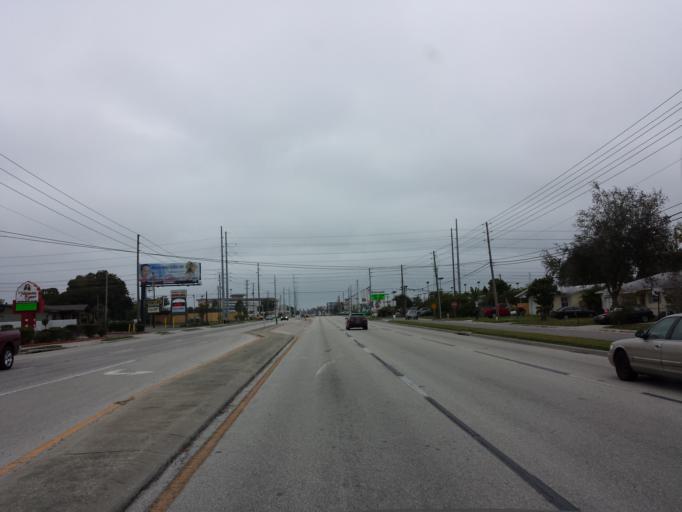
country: US
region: Florida
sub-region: Pinellas County
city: Bay Pines
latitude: 27.8392
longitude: -82.7567
